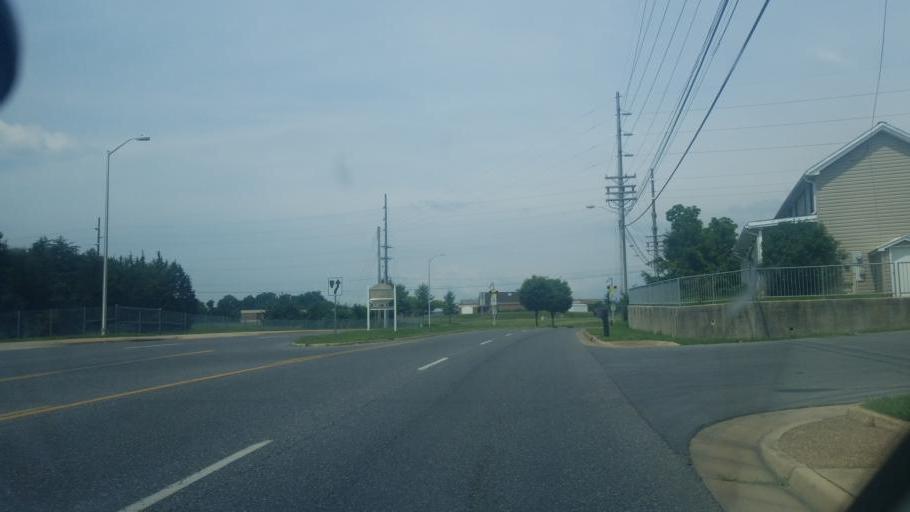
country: US
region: Virginia
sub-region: City of Harrisonburg
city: Harrisonburg
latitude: 38.4521
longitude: -78.8872
